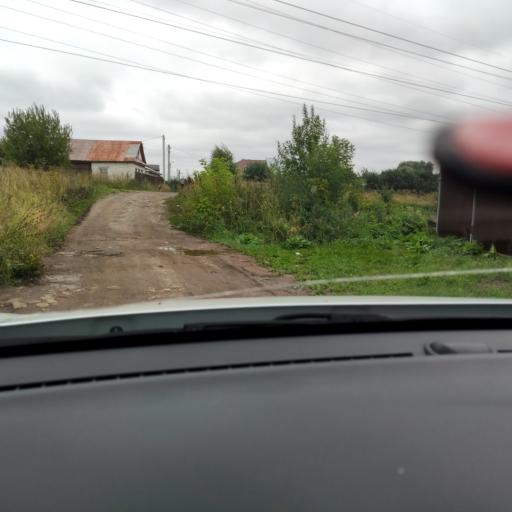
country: RU
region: Tatarstan
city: Stolbishchi
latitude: 55.7455
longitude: 49.3003
